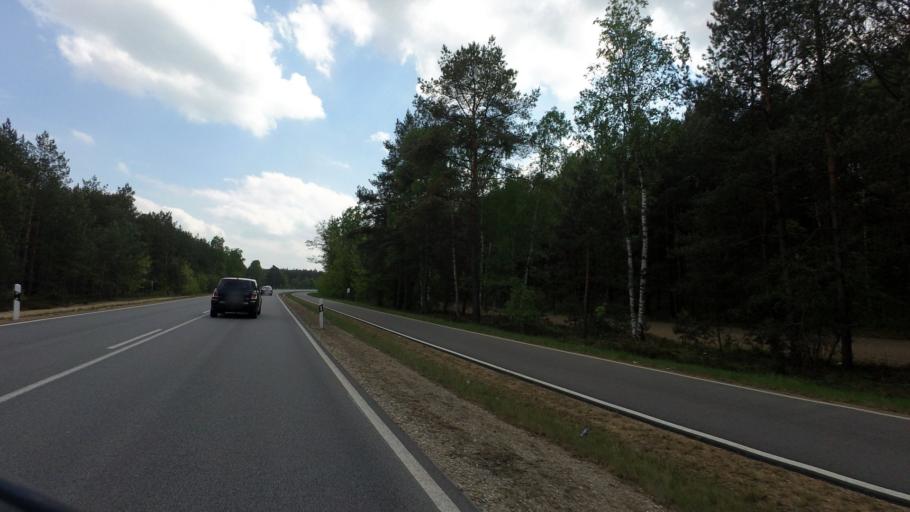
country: DE
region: Saxony
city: Rietschen
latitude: 51.4388
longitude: 14.7824
